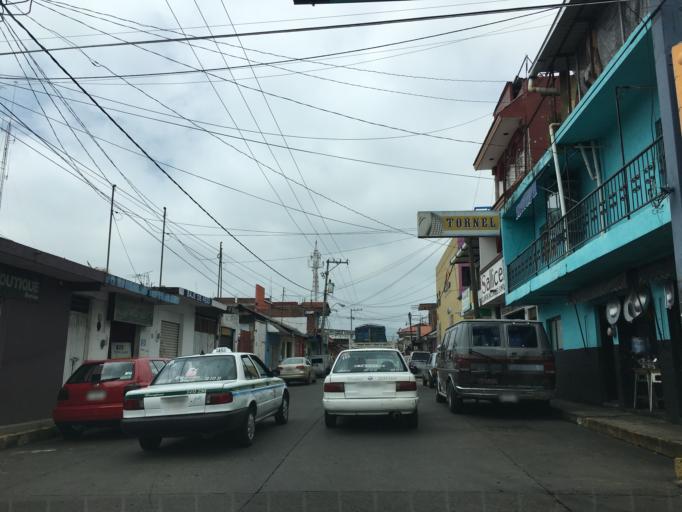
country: MX
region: Michoacan
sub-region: Uruapan
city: Uruapan
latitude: 19.4203
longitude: -102.0540
